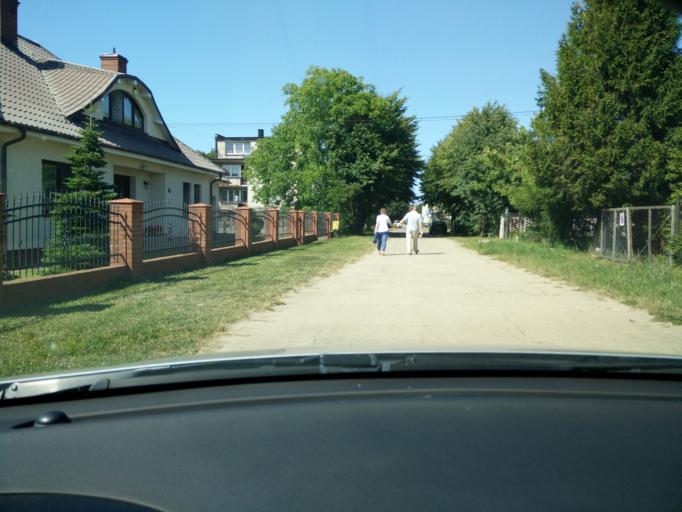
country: PL
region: Pomeranian Voivodeship
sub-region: Powiat pucki
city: Mosty
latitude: 54.6300
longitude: 18.5008
